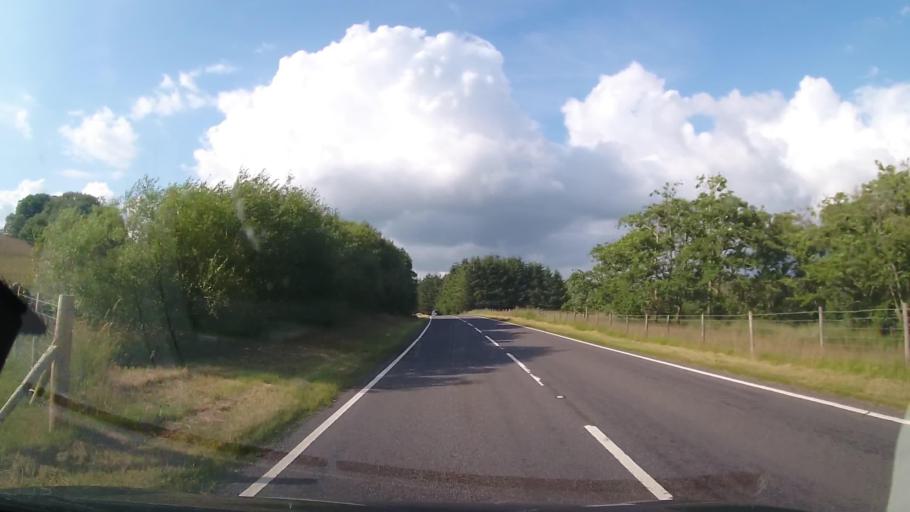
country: GB
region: Wales
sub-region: Gwynedd
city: Bala
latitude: 52.9504
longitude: -3.7189
